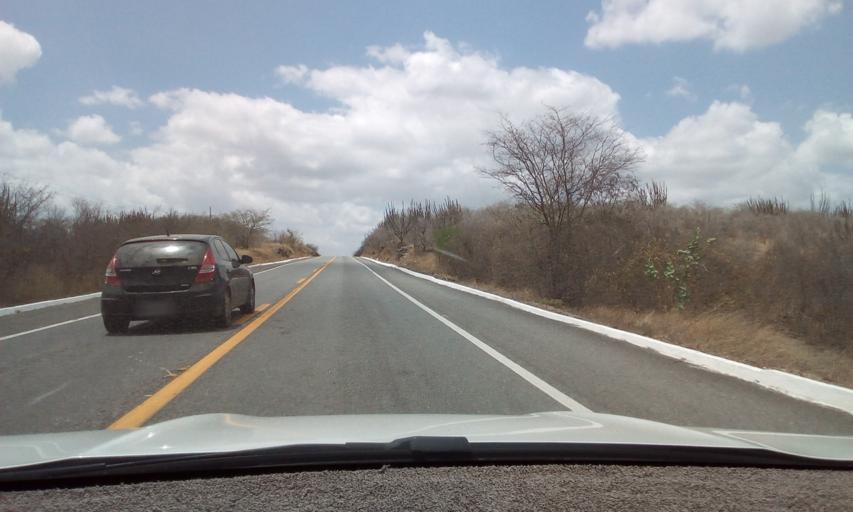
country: BR
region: Paraiba
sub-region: Boqueirao
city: Boqueirao
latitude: -7.6361
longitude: -36.0787
